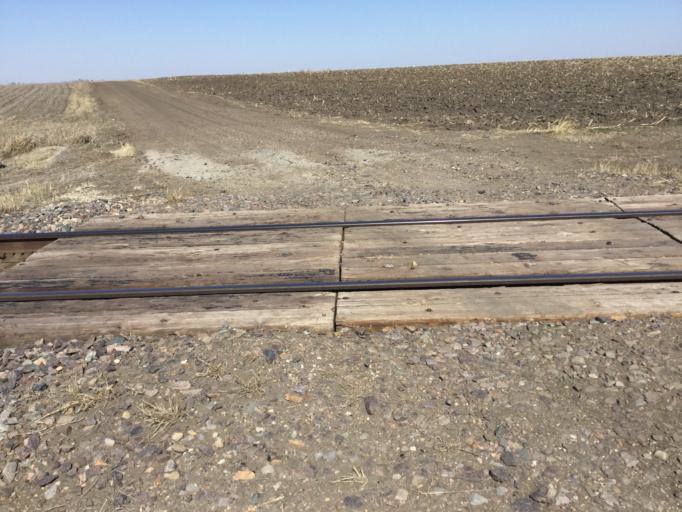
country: US
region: Kansas
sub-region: Nemaha County
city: Seneca
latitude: 39.8965
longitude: -96.3337
